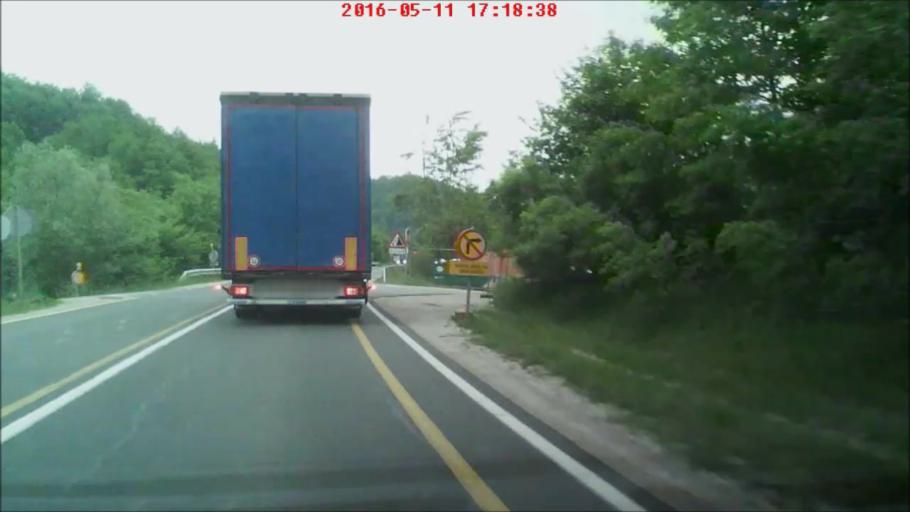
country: SI
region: Podlehnik
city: Podlehnik
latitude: 46.3045
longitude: 15.8601
